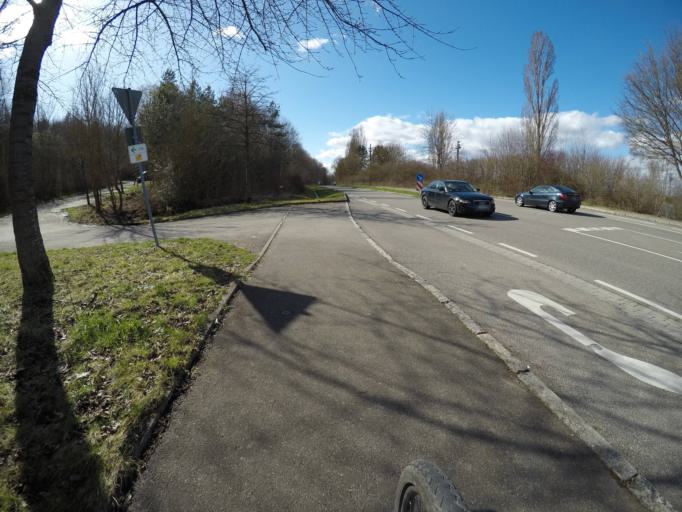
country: DE
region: Baden-Wuerttemberg
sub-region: Regierungsbezirk Stuttgart
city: Leinfelden-Echterdingen
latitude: 48.6869
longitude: 9.1426
